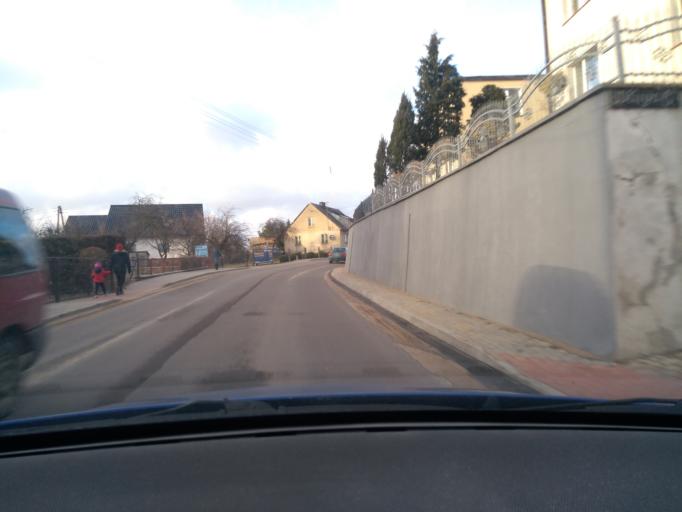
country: PL
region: Pomeranian Voivodeship
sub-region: Powiat kartuski
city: Kartuzy
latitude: 54.3532
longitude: 18.2178
